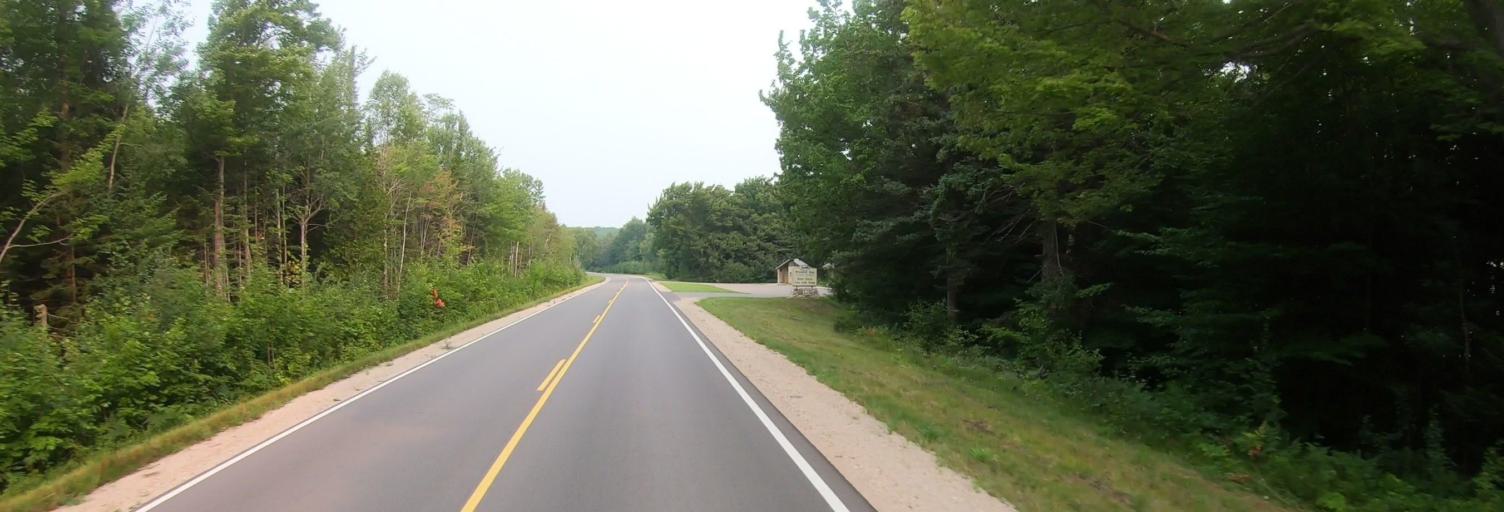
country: US
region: Michigan
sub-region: Luce County
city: Newberry
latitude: 46.4842
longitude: -85.0295
